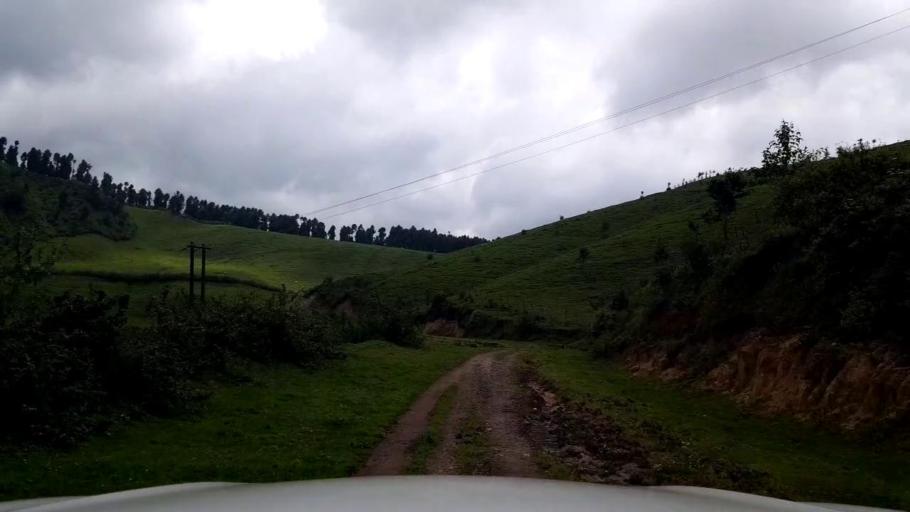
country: RW
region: Western Province
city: Gisenyi
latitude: -1.6903
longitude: 29.4257
